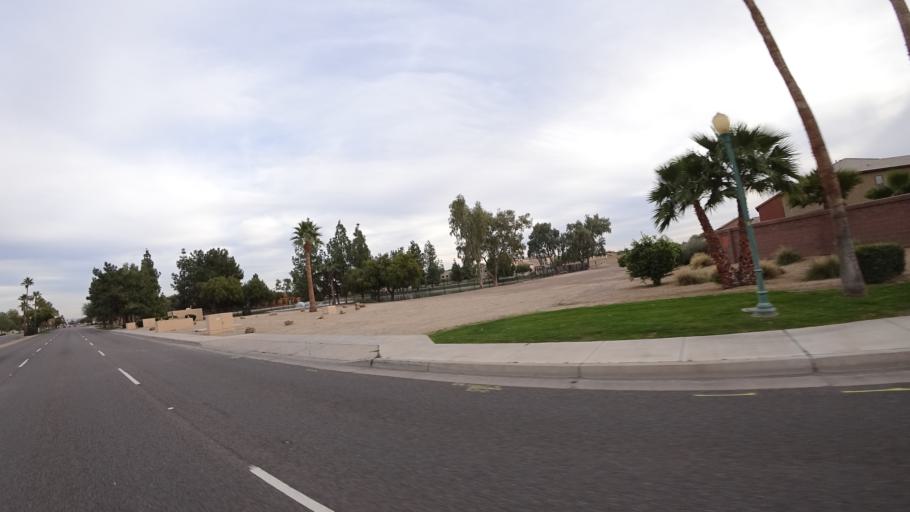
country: US
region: Arizona
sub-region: Maricopa County
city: Sun City West
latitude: 33.6386
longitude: -112.3858
